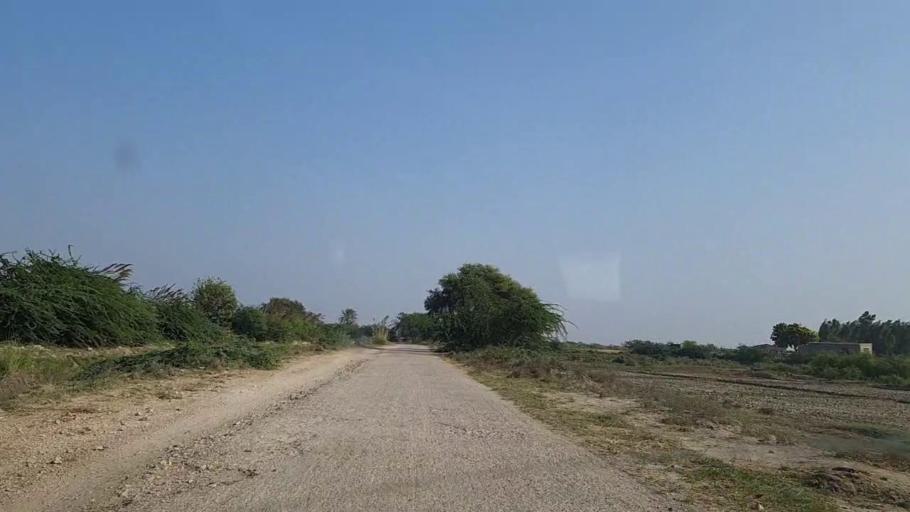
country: PK
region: Sindh
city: Mirpur Sakro
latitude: 24.5956
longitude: 67.5986
